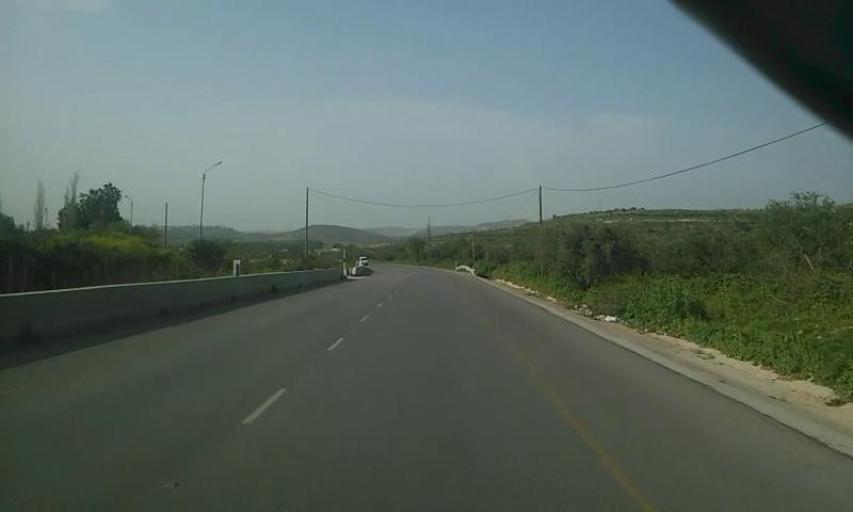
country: PS
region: West Bank
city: Dayr Sharaf
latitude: 32.2588
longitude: 35.1763
